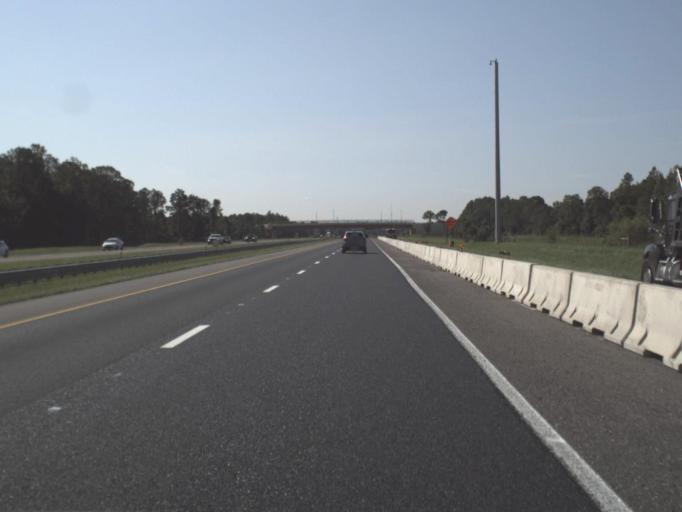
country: US
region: Florida
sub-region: Hillsborough County
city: Pebble Creek
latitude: 28.1488
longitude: -82.3868
